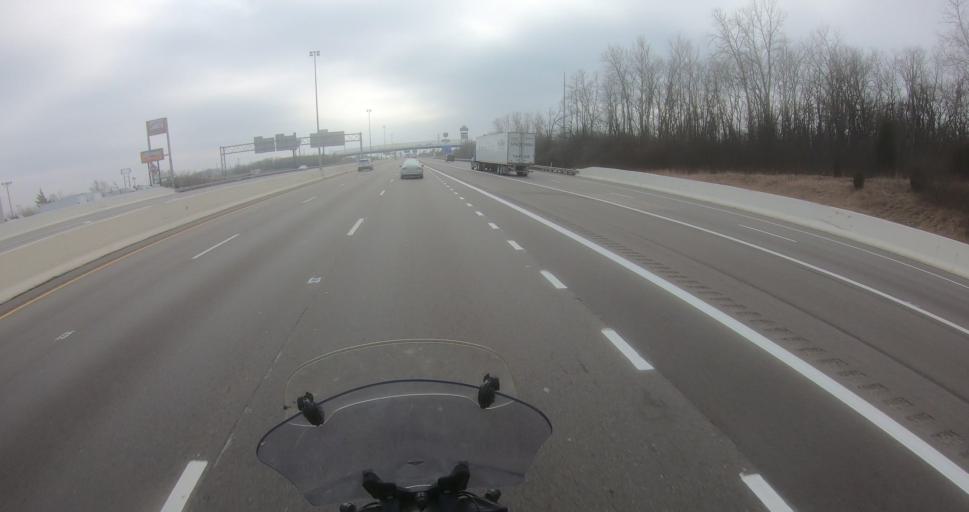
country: US
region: Ohio
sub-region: Montgomery County
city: Vandalia
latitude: 39.8593
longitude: -84.1894
